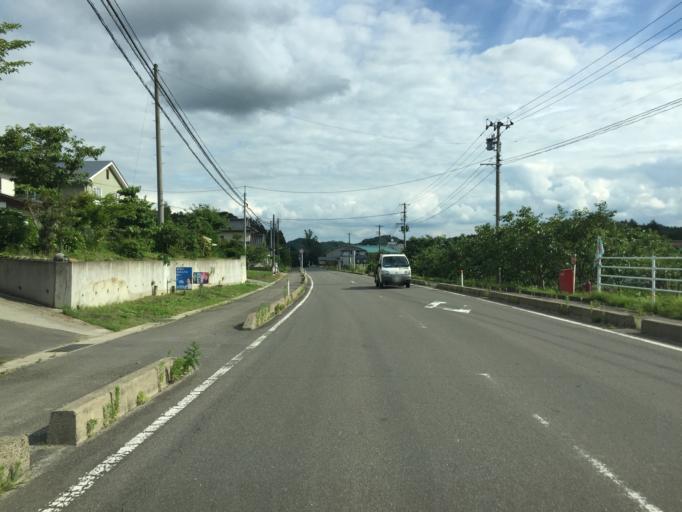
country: JP
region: Fukushima
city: Fukushima-shi
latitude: 37.6633
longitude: 140.5316
